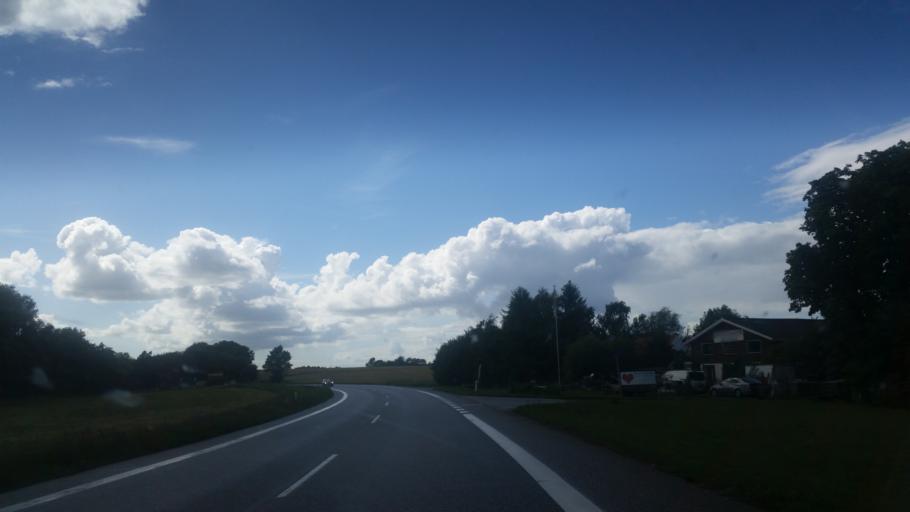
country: DK
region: Zealand
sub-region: Holbaek Kommune
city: Svinninge
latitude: 55.7275
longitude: 11.5774
